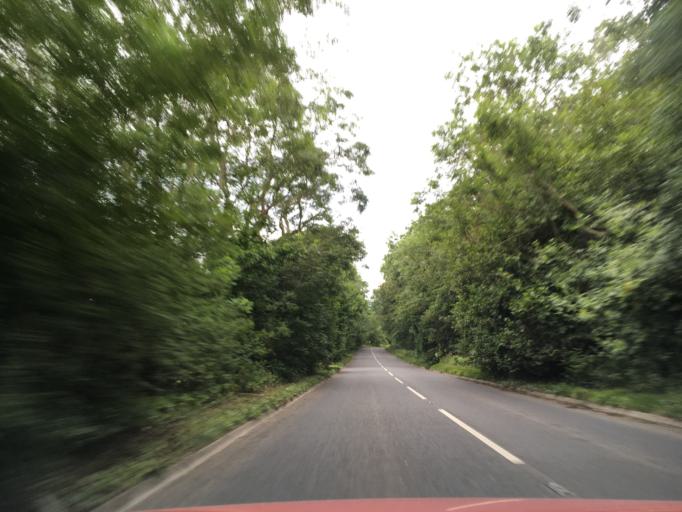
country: GB
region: England
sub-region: North Somerset
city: Long Ashton
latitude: 51.4320
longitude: -2.6960
